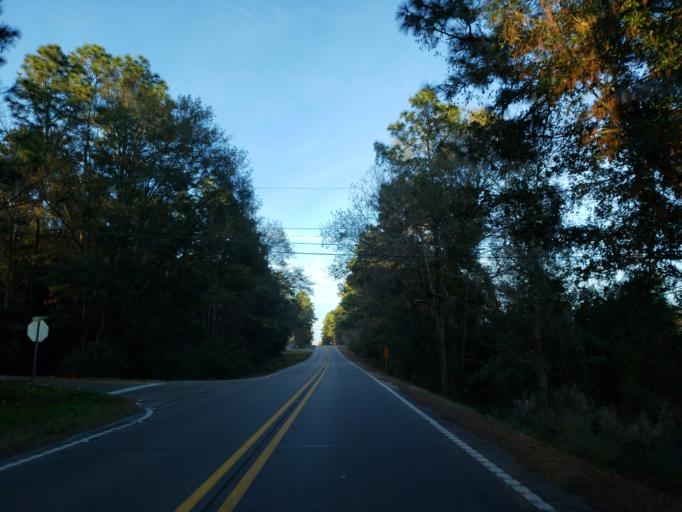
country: US
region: Mississippi
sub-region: Lamar County
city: Purvis
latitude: 31.1545
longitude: -89.3978
